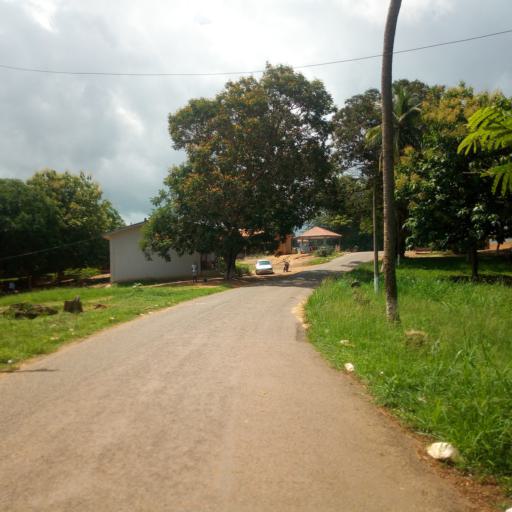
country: GH
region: Western
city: Sekondi-Takoradi
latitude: 4.9311
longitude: -1.7461
